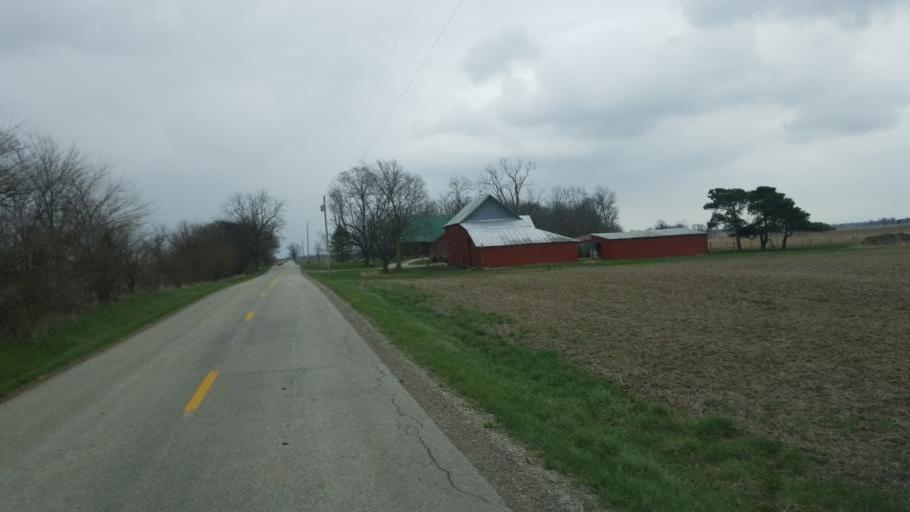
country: US
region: Ohio
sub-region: Marion County
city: Prospect
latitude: 40.4187
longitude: -83.1826
